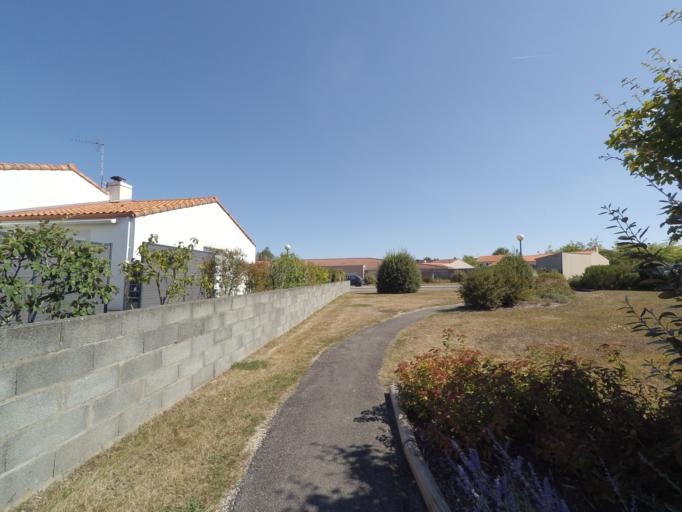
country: FR
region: Pays de la Loire
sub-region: Departement de la Loire-Atlantique
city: Vieillevigne
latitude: 46.9721
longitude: -1.4382
